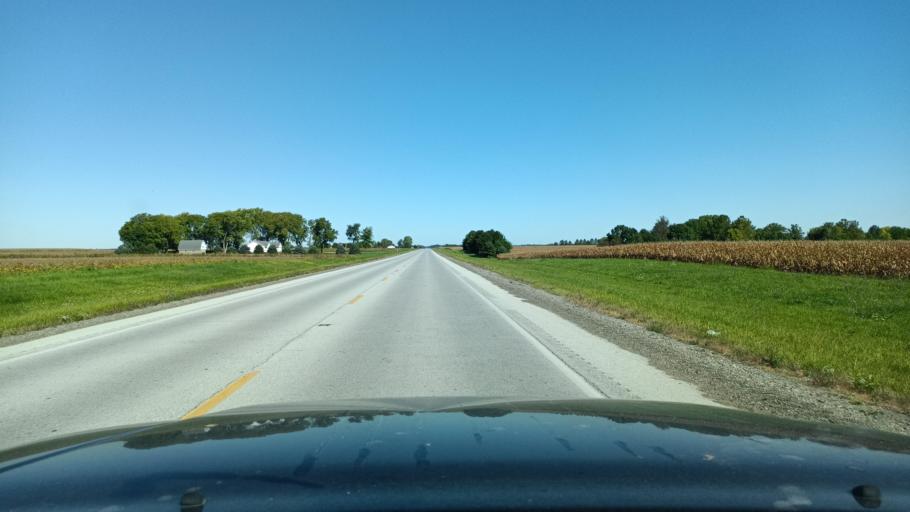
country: US
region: Illinois
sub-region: Champaign County
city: Philo
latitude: 40.0311
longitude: -88.1616
